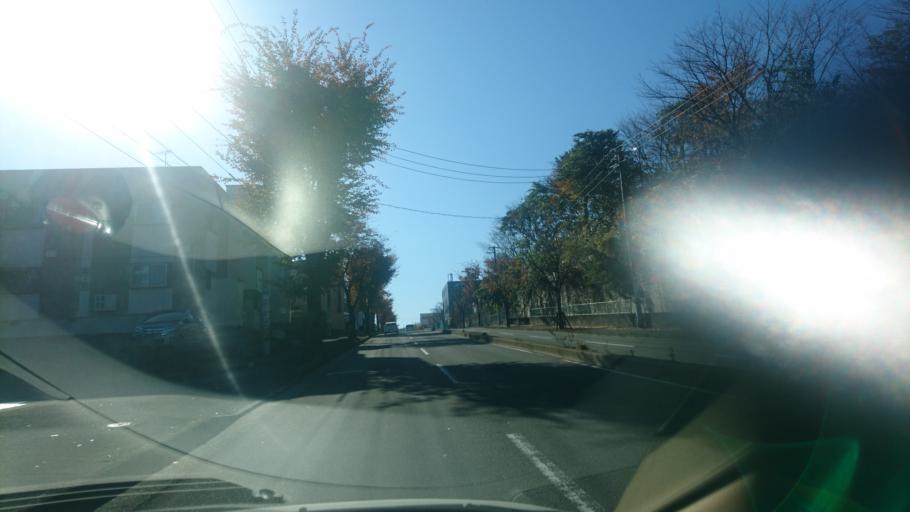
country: JP
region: Miyagi
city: Sendai-shi
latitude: 38.3033
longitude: 140.8310
